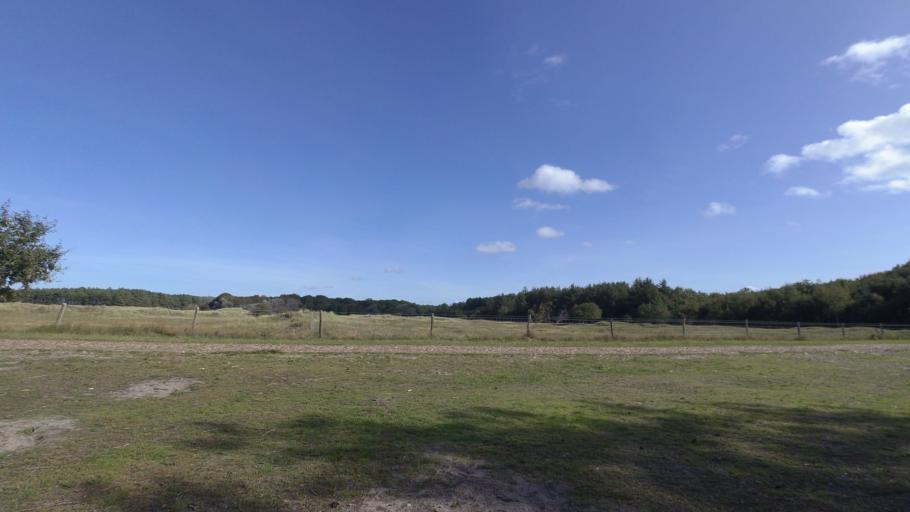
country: NL
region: Friesland
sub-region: Gemeente Ameland
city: Hollum
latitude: 53.4477
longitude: 5.7041
